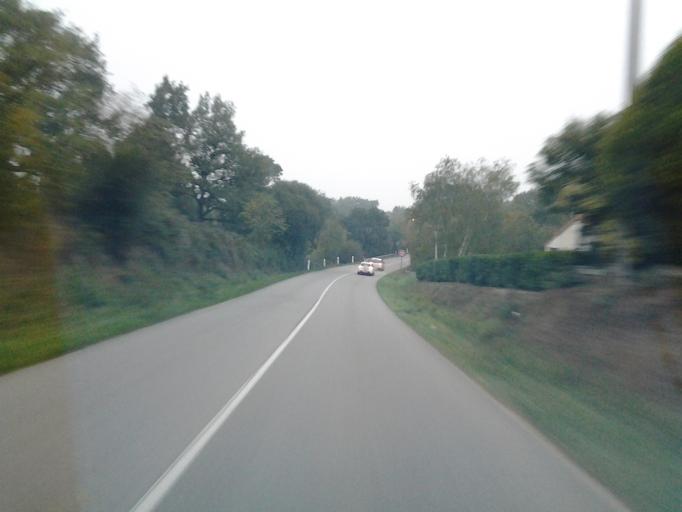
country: FR
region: Pays de la Loire
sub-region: Departement de la Vendee
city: La Roche-sur-Yon
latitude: 46.6453
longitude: -1.4206
